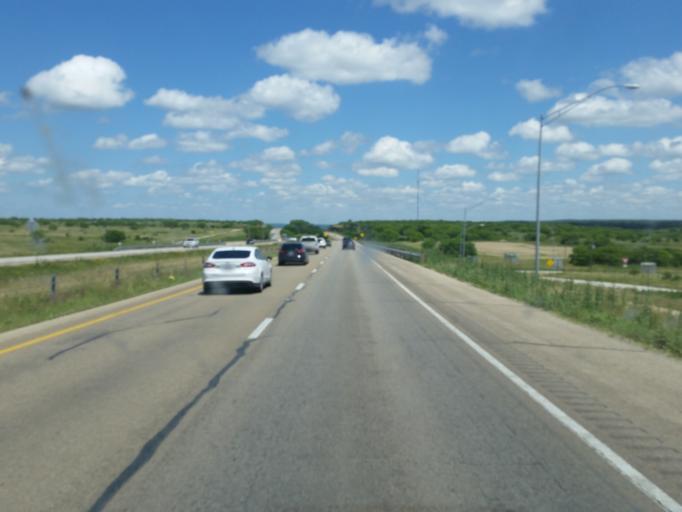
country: US
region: Texas
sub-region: Callahan County
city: Baird
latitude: 32.3988
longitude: -99.3755
